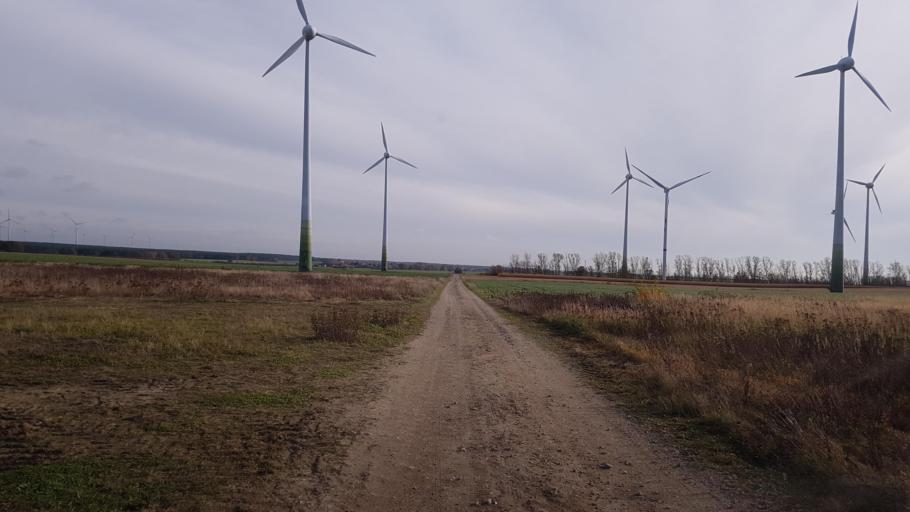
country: DE
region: Brandenburg
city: Treuenbrietzen
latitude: 52.0164
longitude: 12.8930
